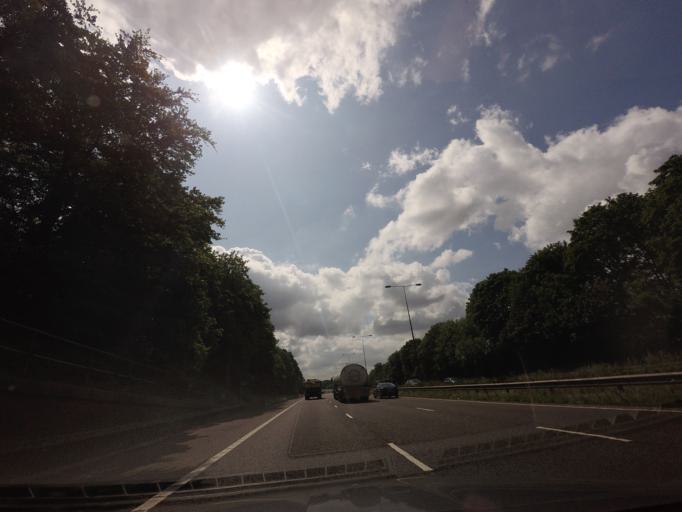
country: GB
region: England
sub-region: Borough of Wigan
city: Shevington
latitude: 53.5375
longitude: -2.6971
